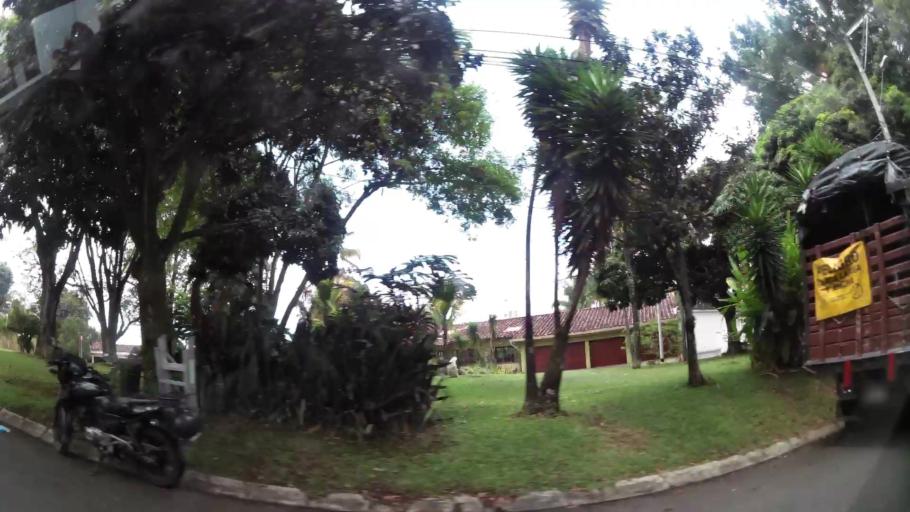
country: CO
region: Antioquia
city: Envigado
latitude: 6.1874
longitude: -75.5747
